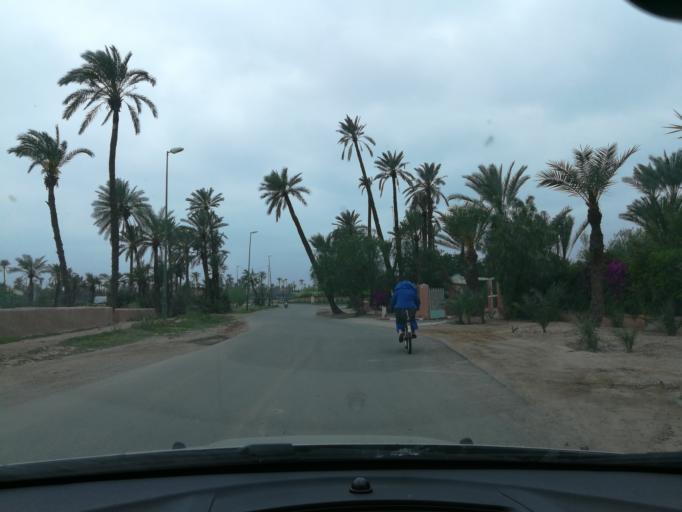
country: MA
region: Marrakech-Tensift-Al Haouz
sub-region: Marrakech
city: Marrakesh
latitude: 31.6791
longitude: -7.9851
